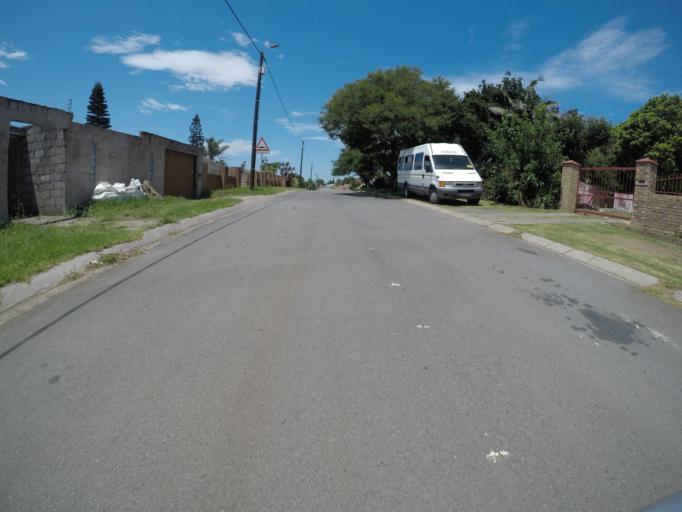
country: ZA
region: Eastern Cape
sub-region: Buffalo City Metropolitan Municipality
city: East London
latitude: -33.0315
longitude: 27.8506
